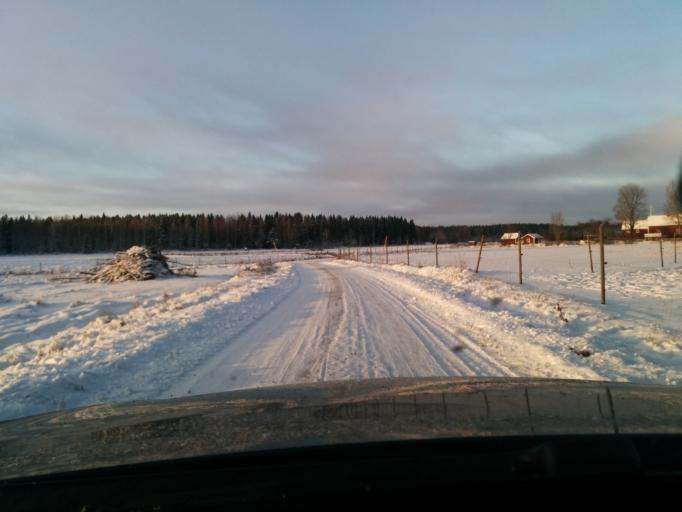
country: SE
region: Uppsala
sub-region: Tierps Kommun
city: Orbyhus
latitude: 60.1937
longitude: 17.6000
